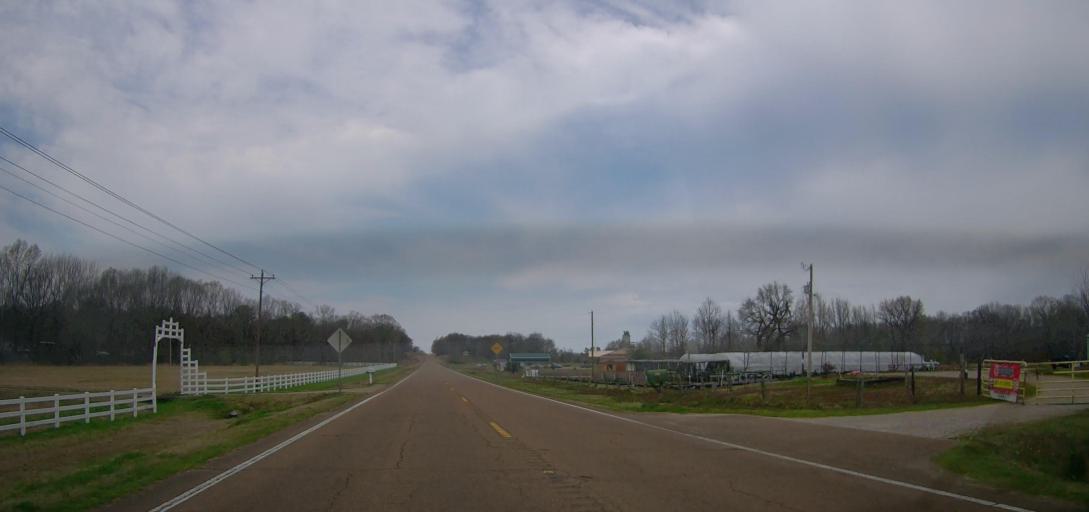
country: US
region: Mississippi
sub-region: Marshall County
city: Byhalia
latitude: 34.8560
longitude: -89.6438
